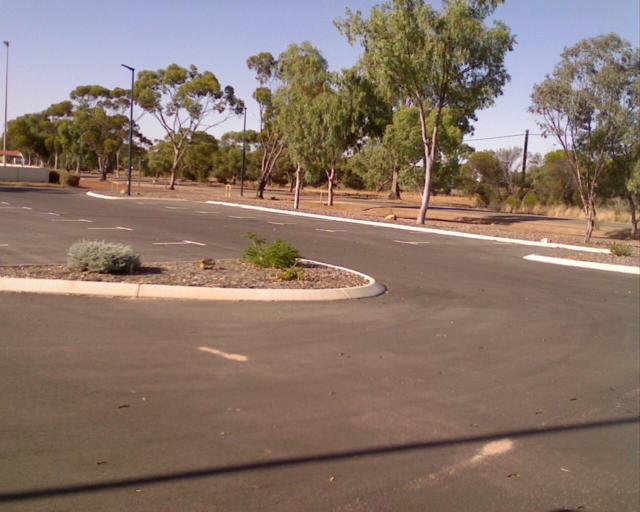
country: AU
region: Western Australia
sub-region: Merredin
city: Merredin
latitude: -31.1114
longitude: 117.7925
